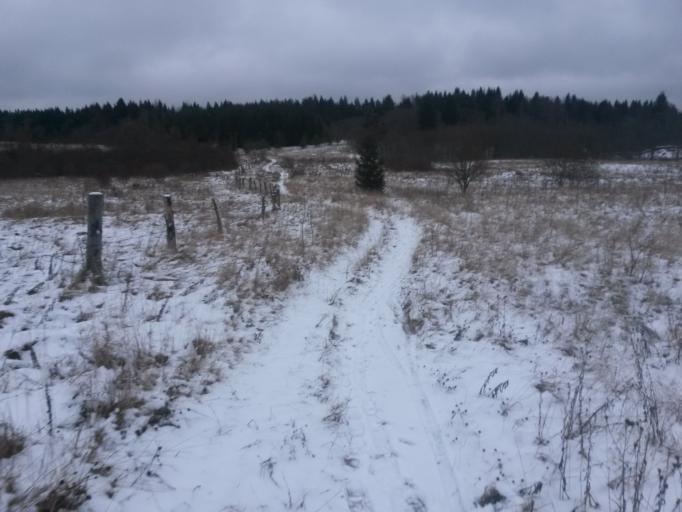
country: RU
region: Novgorod
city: Valday
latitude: 57.9454
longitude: 33.0016
